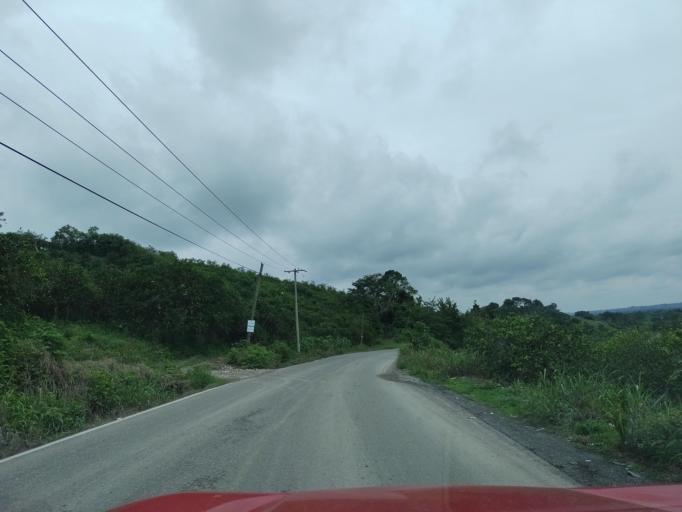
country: MX
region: Puebla
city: Espinal
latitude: 20.2626
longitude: -97.3640
